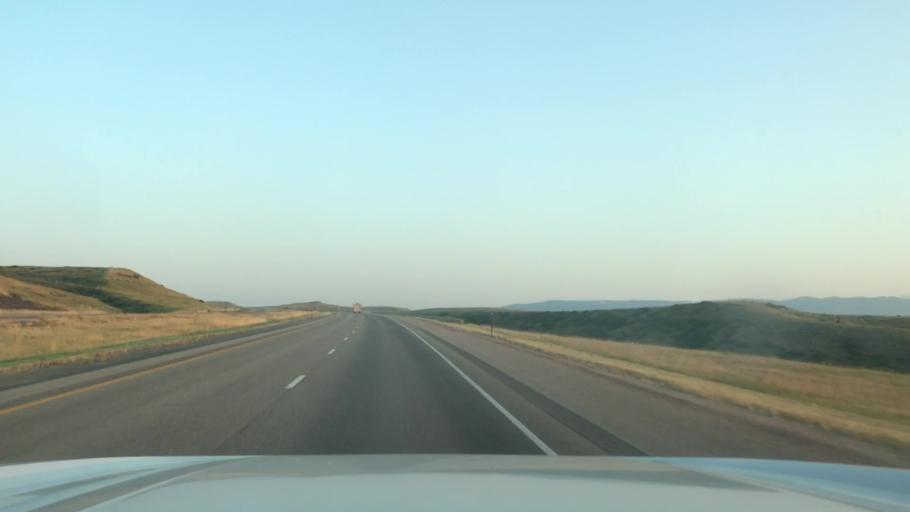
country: US
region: Wyoming
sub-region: Sheridan County
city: Sheridan
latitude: 44.7268
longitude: -106.9188
